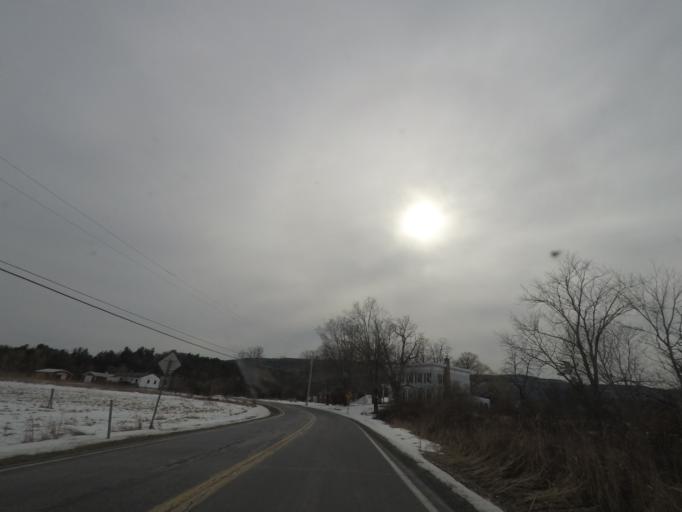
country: US
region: New York
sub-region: Albany County
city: Voorheesville
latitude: 42.6657
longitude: -73.9860
